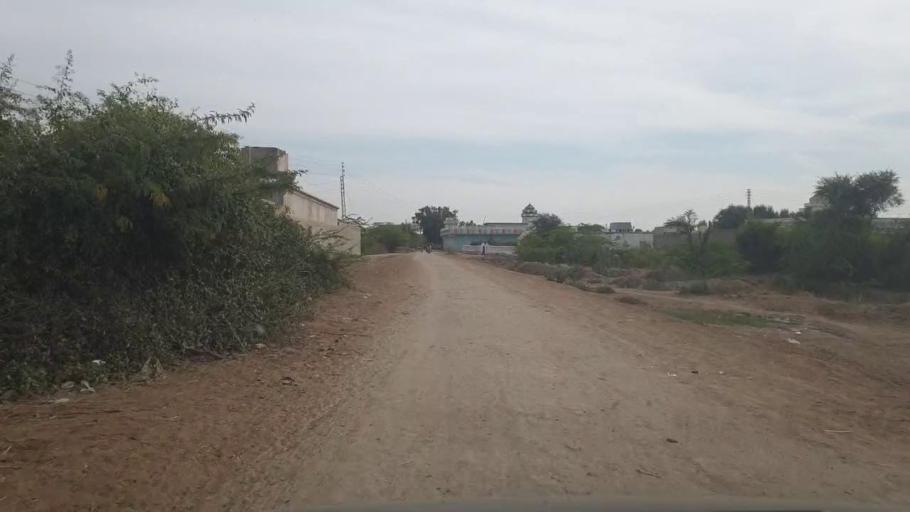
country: PK
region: Sindh
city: Kunri
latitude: 25.2855
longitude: 69.5983
